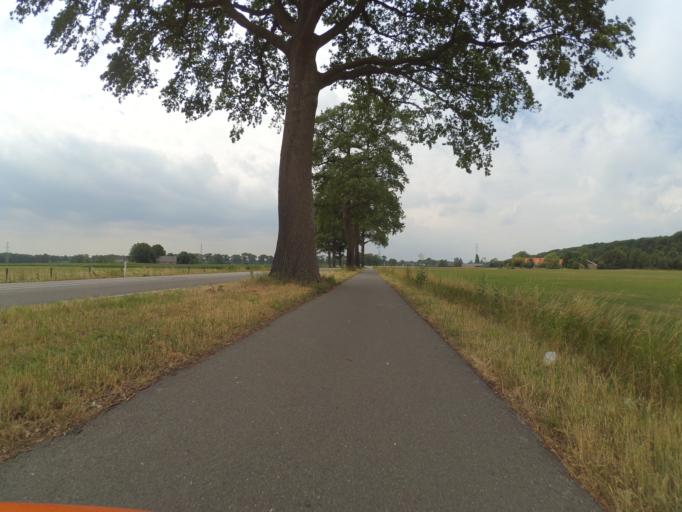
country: NL
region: Gelderland
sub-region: Gemeente Lochem
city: Lochem
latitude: 52.1685
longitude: 6.4527
